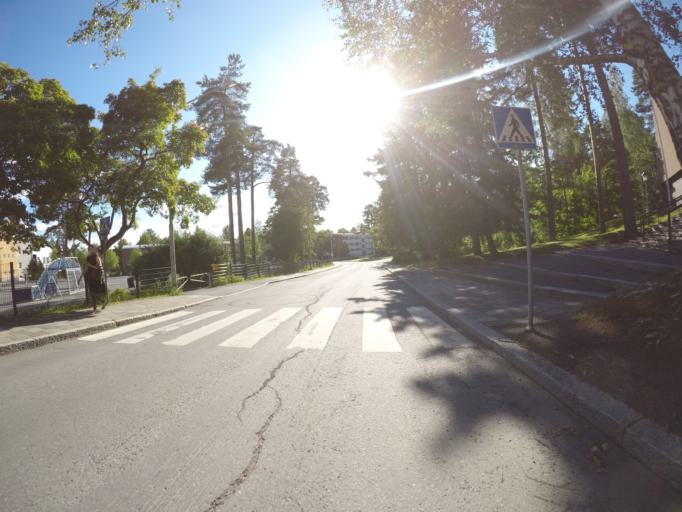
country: FI
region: Haeme
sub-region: Haemeenlinna
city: Haemeenlinna
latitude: 61.0070
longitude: 24.4814
